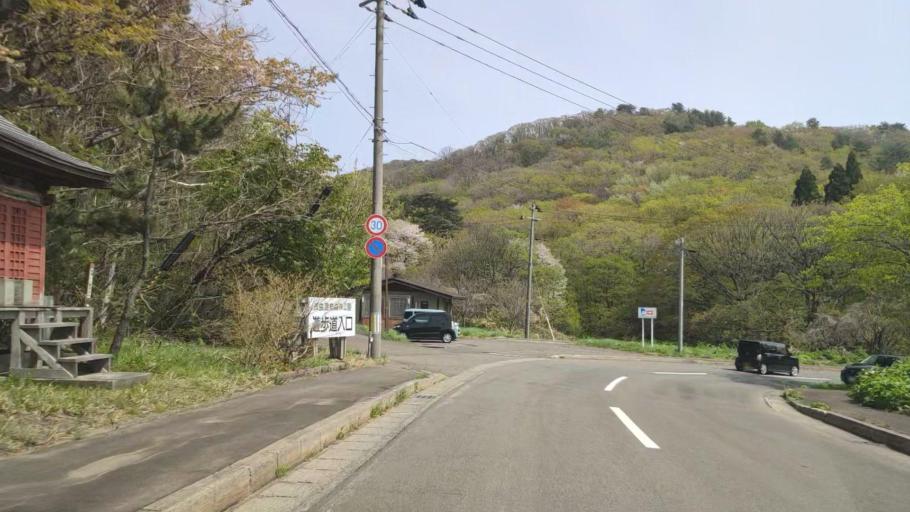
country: JP
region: Aomori
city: Aomori Shi
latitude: 40.9015
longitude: 140.8639
